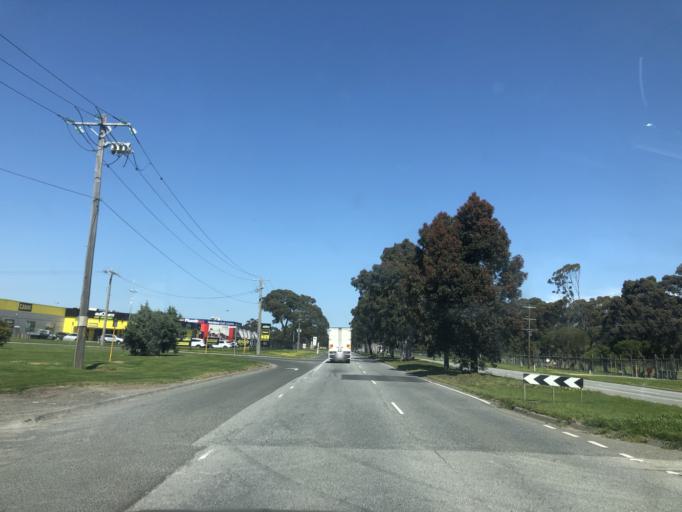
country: AU
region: Victoria
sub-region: Casey
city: Doveton
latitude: -38.0179
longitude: 145.2148
